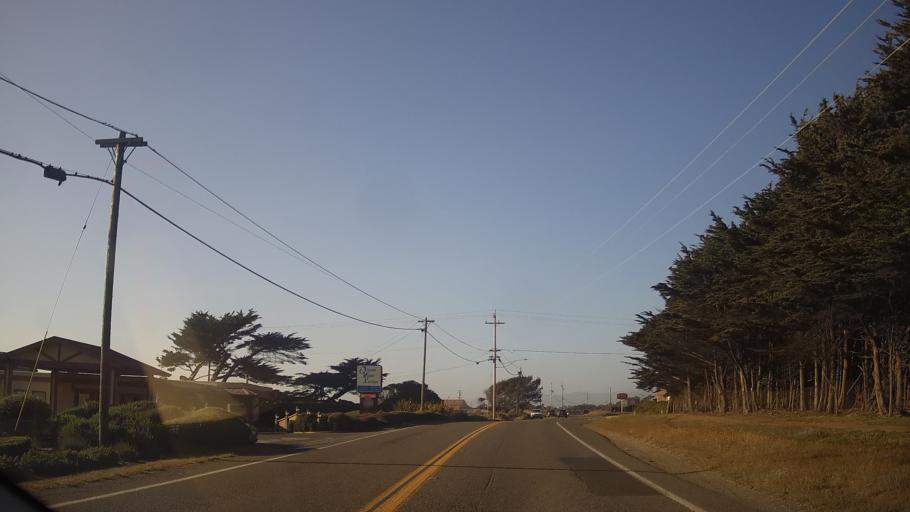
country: US
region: California
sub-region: Mendocino County
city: Fort Bragg
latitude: 39.4624
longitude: -123.8060
